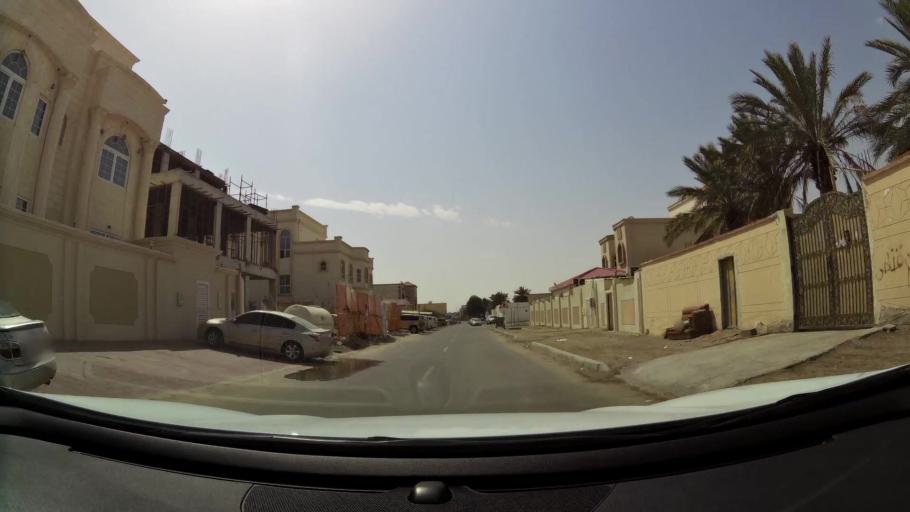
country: AE
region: Abu Dhabi
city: Abu Dhabi
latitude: 24.2896
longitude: 54.6542
